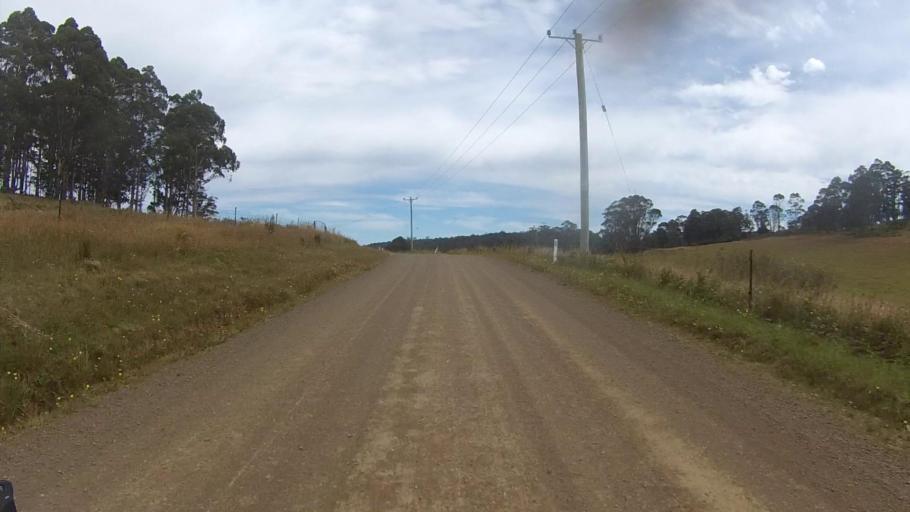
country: AU
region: Tasmania
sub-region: Sorell
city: Sorell
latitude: -42.7229
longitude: 147.7516
